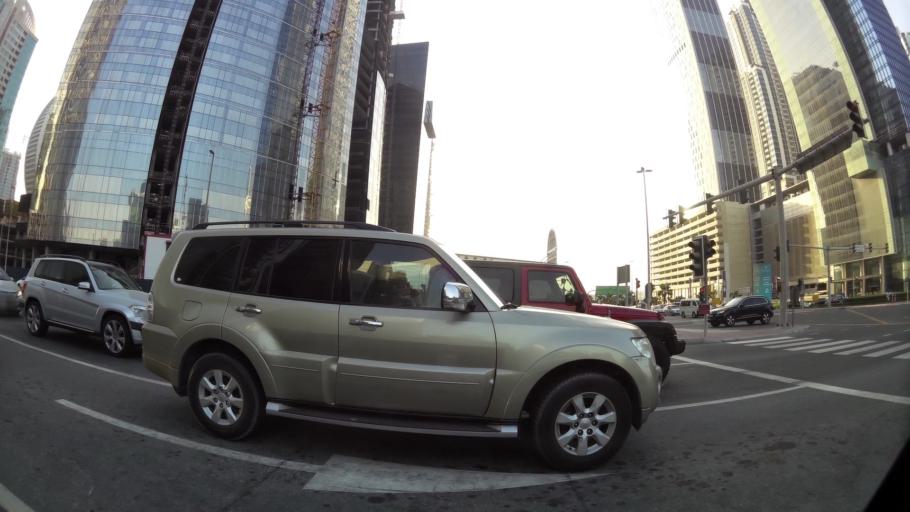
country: AE
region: Dubai
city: Dubai
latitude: 25.1871
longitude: 55.2637
